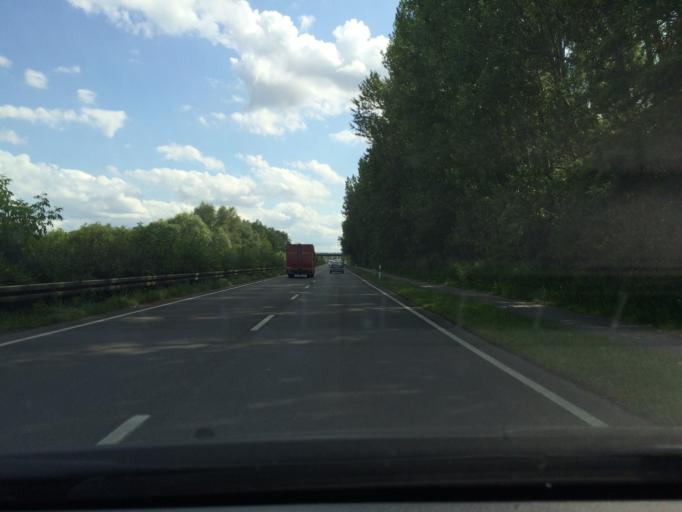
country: DE
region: Mecklenburg-Vorpommern
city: Lambrechtshagen
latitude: 54.1208
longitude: 12.0651
